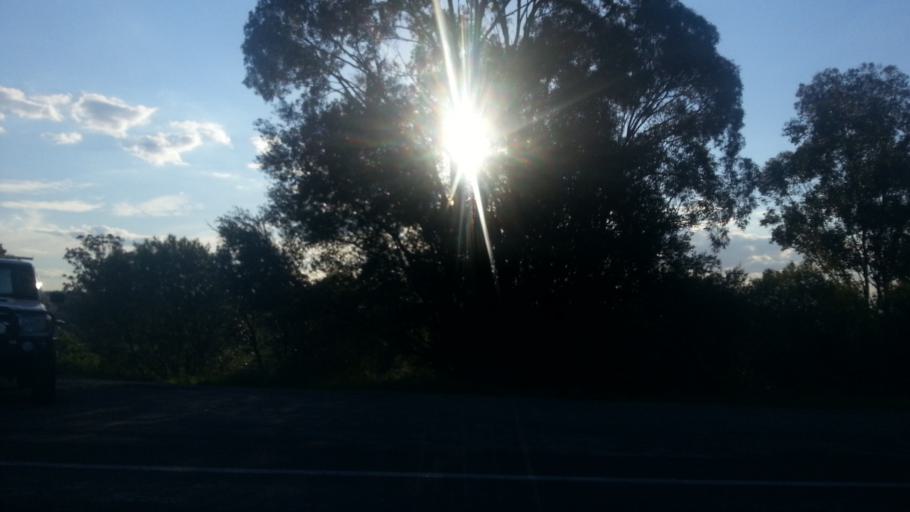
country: AU
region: New South Wales
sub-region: Camden
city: Camden South
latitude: -34.0987
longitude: 150.6953
